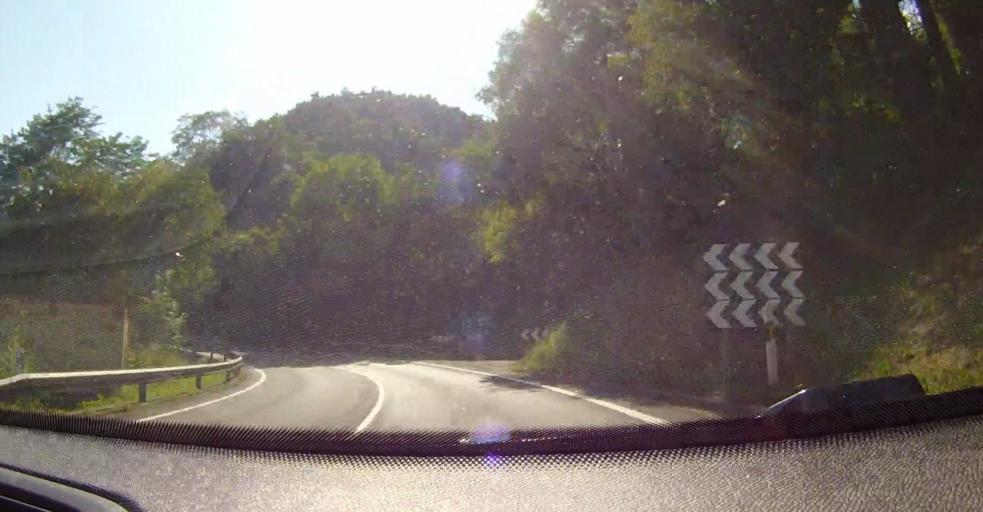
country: ES
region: Basque Country
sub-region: Bizkaia
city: Muxika
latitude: 43.2615
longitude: -2.6878
